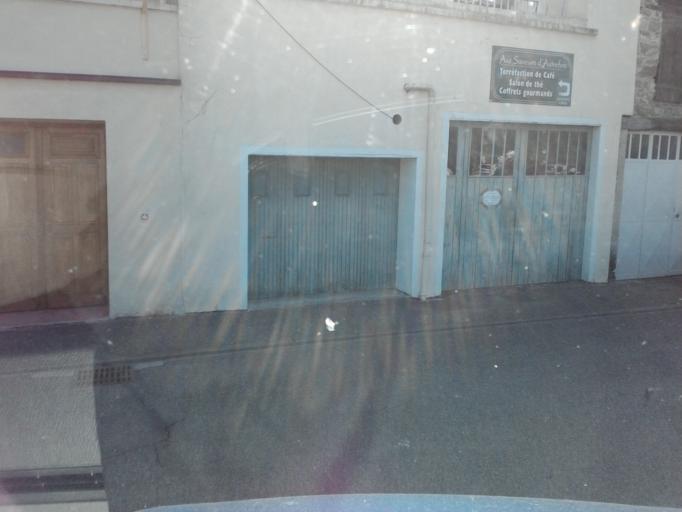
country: FR
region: Rhone-Alpes
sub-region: Departement de l'Ain
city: Lagnieu
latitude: 45.9026
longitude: 5.3464
